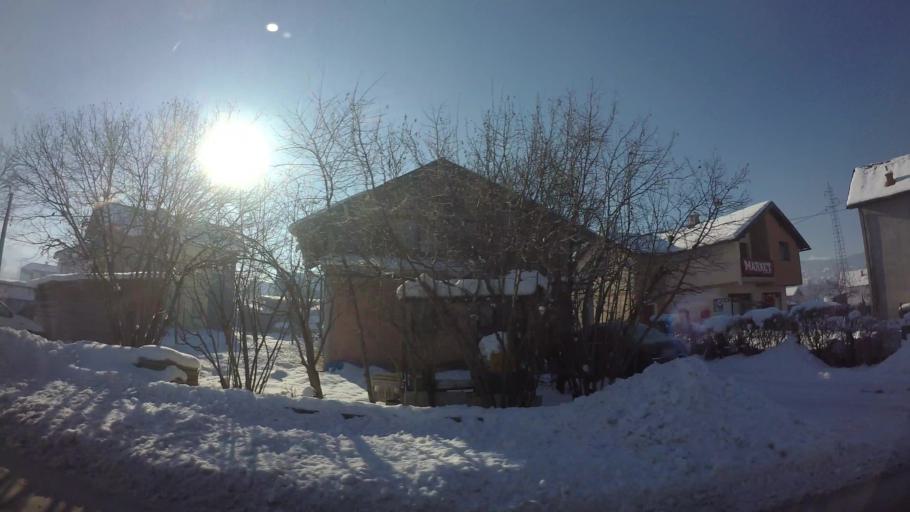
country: BA
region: Federation of Bosnia and Herzegovina
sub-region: Kanton Sarajevo
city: Sarajevo
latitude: 43.8212
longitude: 18.3788
